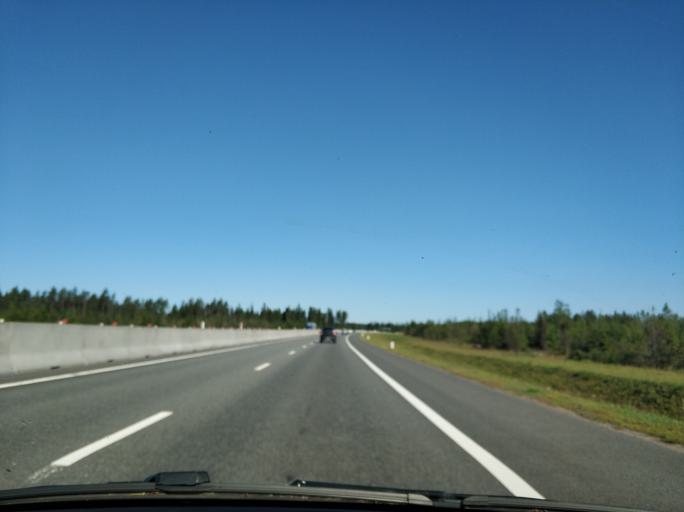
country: RU
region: Leningrad
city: Sosnovo
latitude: 60.4402
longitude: 30.2145
